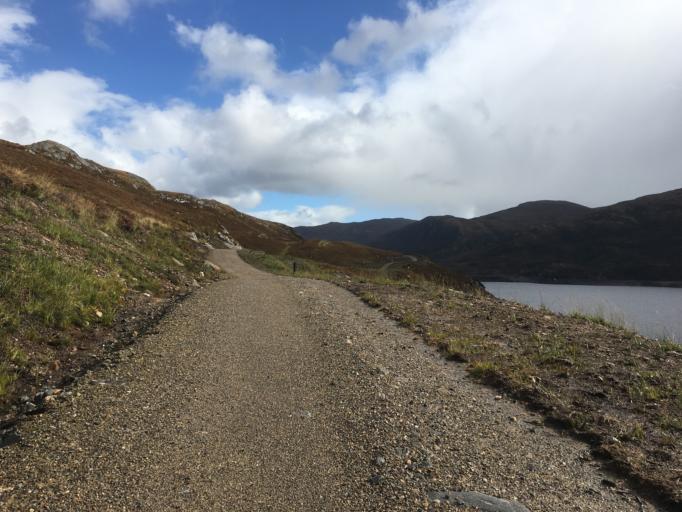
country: GB
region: Scotland
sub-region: Highland
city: Spean Bridge
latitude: 57.3411
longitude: -4.9767
